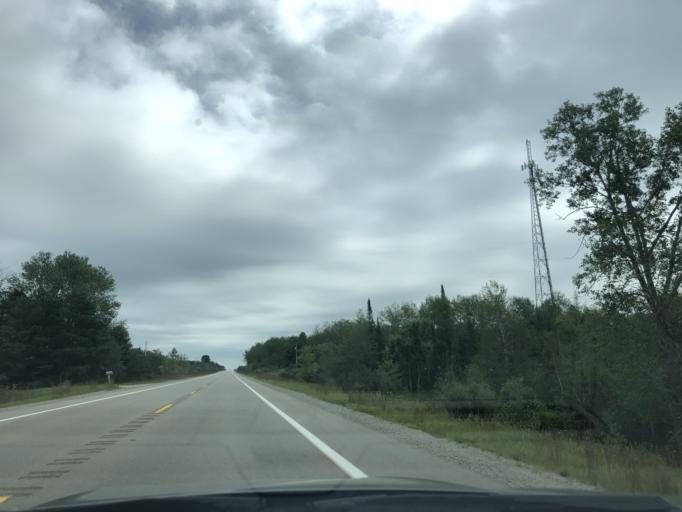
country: US
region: Michigan
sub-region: Clare County
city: Harrison
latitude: 44.0311
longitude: -84.9747
